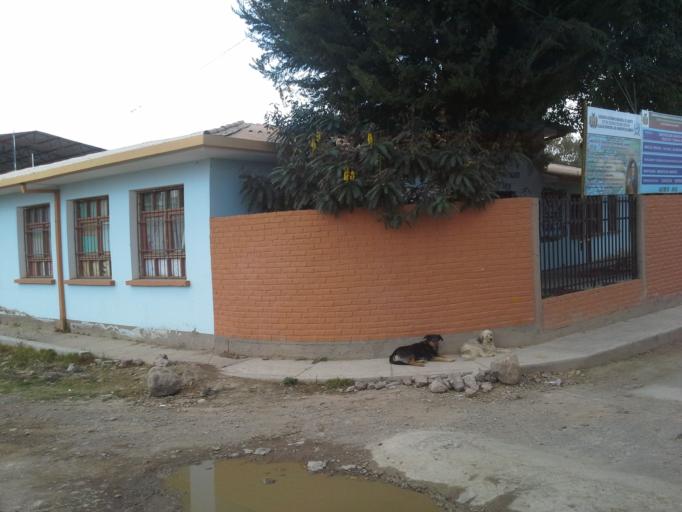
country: BO
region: Cochabamba
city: Tarata
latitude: -17.5857
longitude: -66.0170
